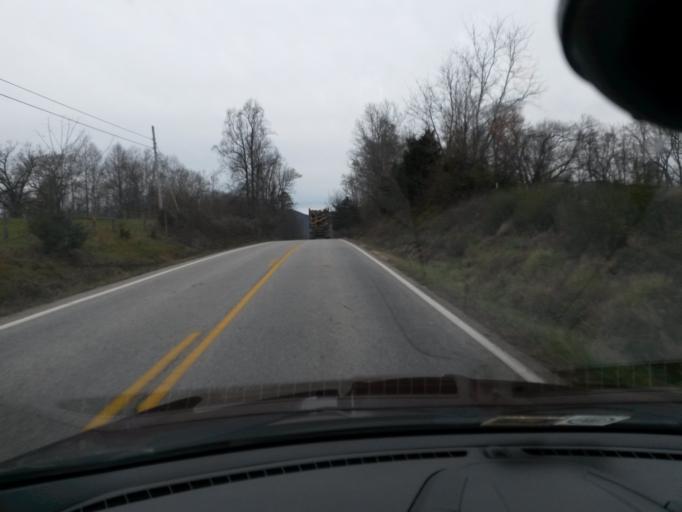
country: US
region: Virginia
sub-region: Amherst County
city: Amherst
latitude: 37.6544
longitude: -79.1379
